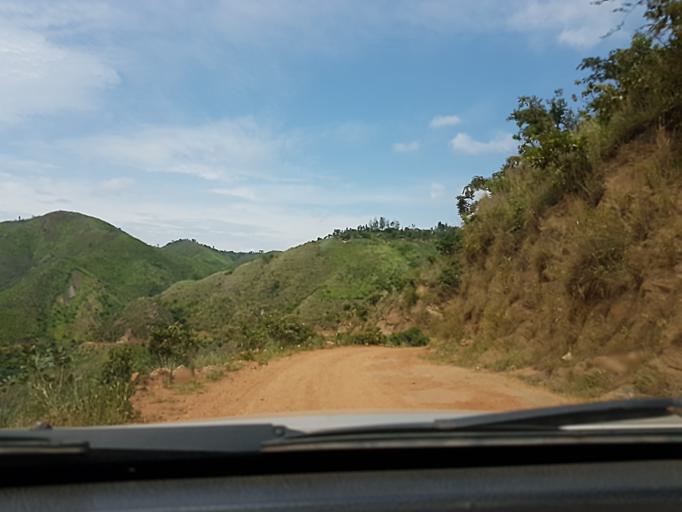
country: RW
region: Western Province
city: Cyangugu
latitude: -2.7058
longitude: 28.9491
